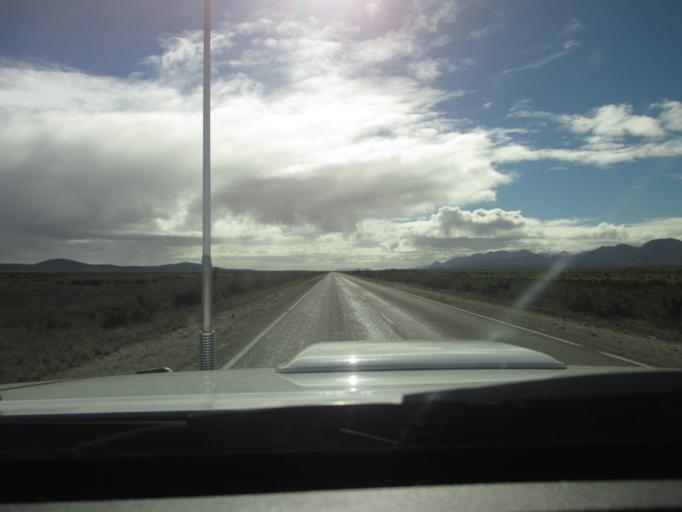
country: AU
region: South Australia
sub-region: Flinders Ranges
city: Quorn
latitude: -31.6889
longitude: 138.3623
